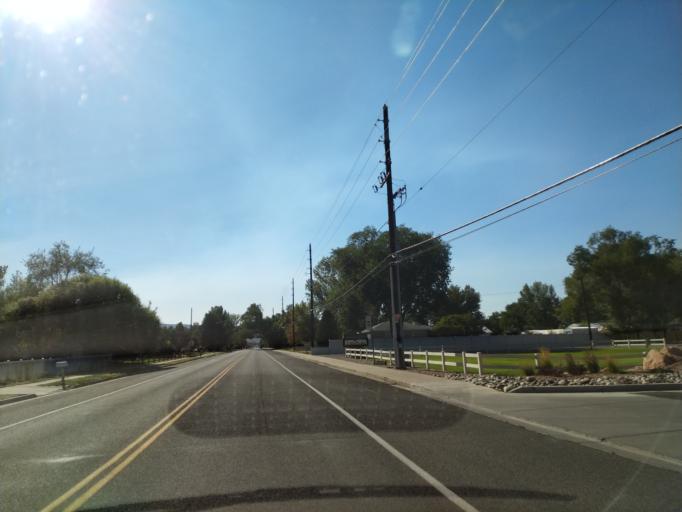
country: US
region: Colorado
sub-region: Mesa County
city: Orchard Mesa
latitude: 39.0412
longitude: -108.5187
